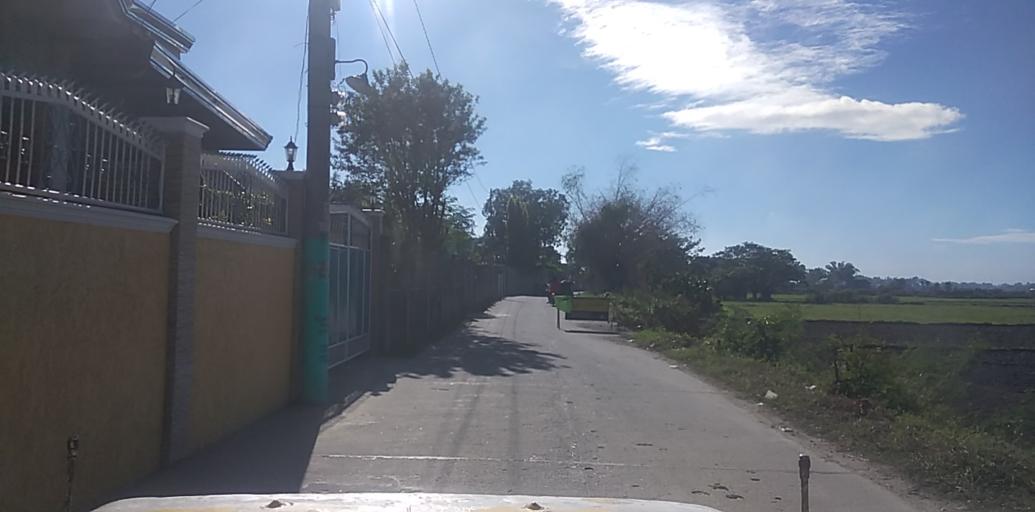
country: PH
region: Central Luzon
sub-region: Province of Pampanga
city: San Patricio
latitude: 15.1147
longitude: 120.7096
